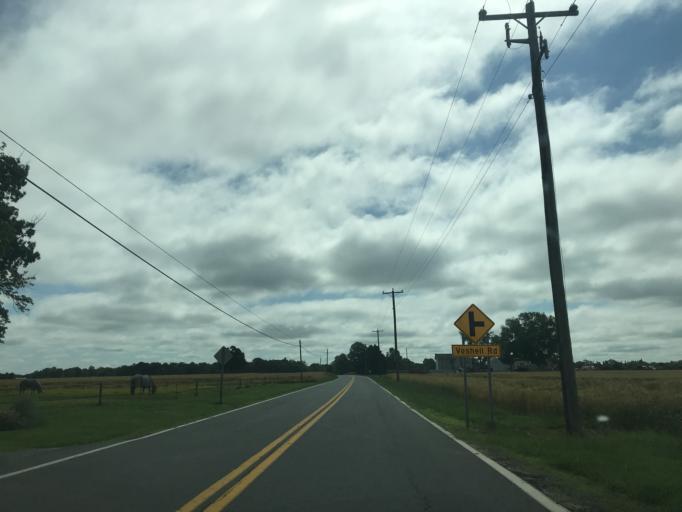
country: US
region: Maryland
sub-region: Caroline County
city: Ridgely
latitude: 38.8851
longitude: -75.9782
